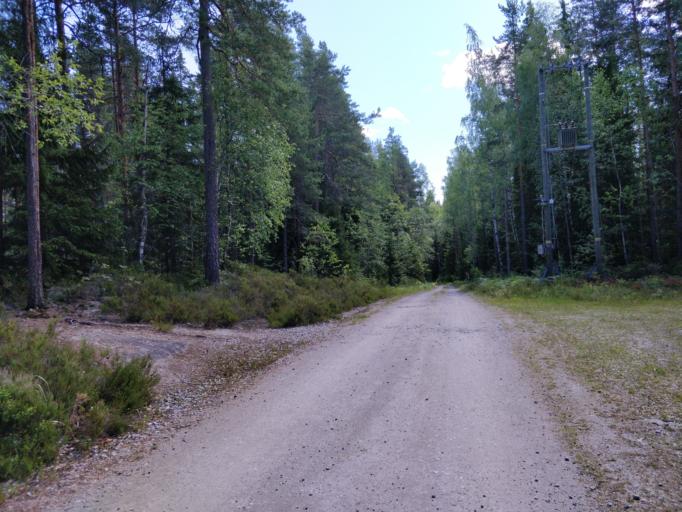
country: FI
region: Uusimaa
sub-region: Helsinki
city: Vihti
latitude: 60.3135
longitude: 24.4608
